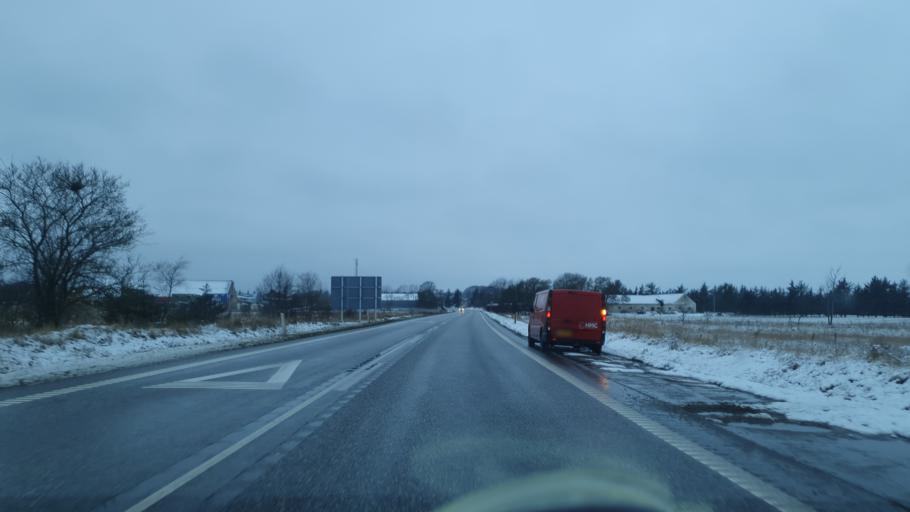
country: DK
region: North Denmark
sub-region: Alborg Kommune
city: Vestbjerg
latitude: 57.0886
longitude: 9.9559
